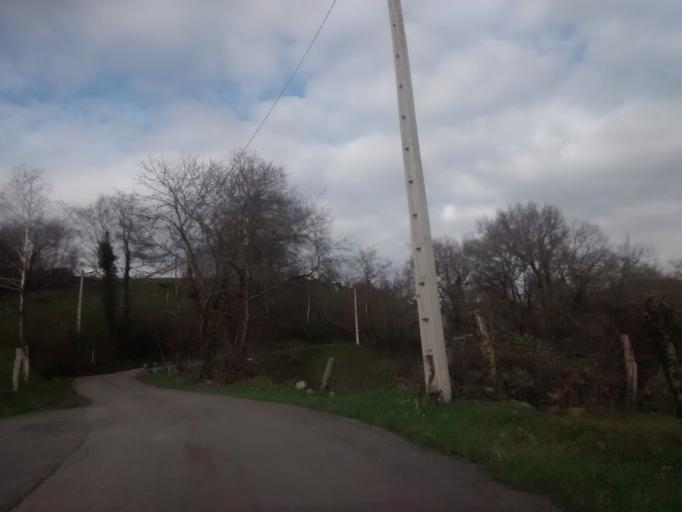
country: ES
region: Cantabria
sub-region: Provincia de Cantabria
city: Entrambasaguas
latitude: 43.3339
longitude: -3.6596
